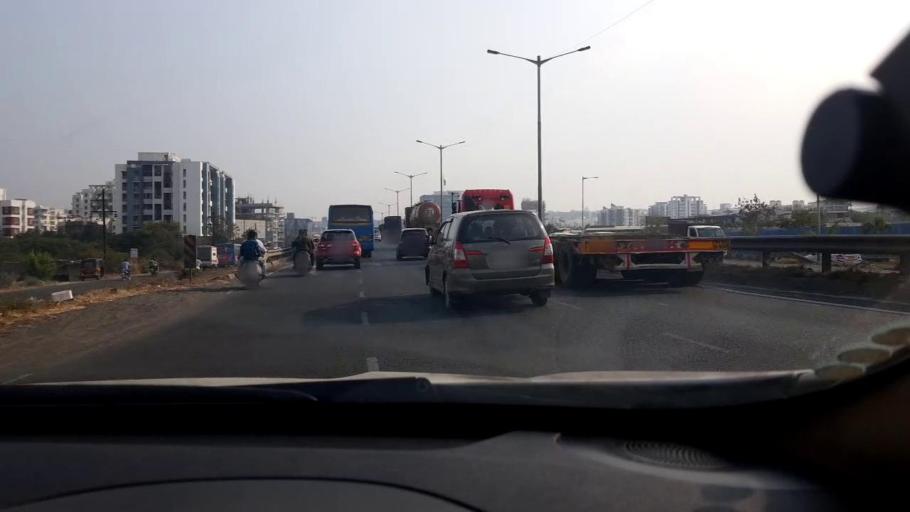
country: IN
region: Maharashtra
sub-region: Pune Division
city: Pimpri
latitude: 18.5628
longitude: 73.7682
